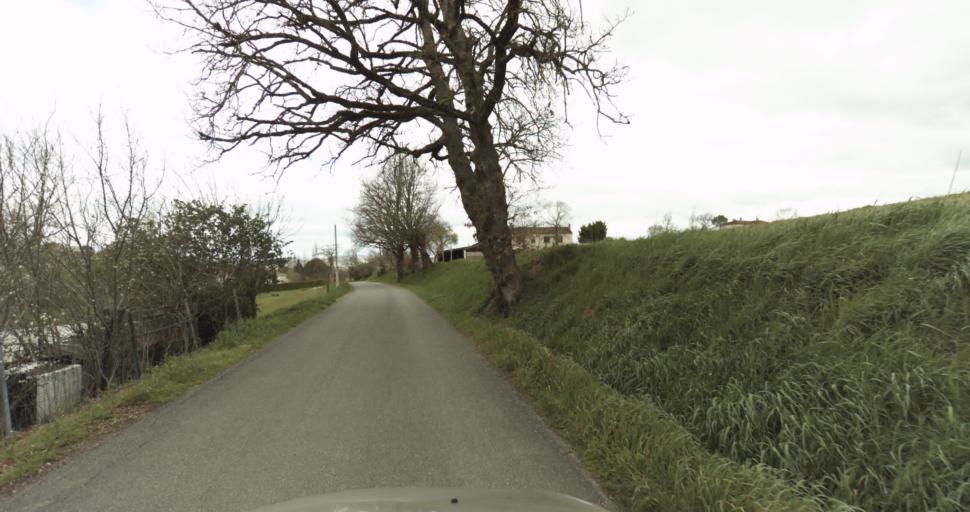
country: FR
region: Midi-Pyrenees
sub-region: Departement du Tarn
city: Puygouzon
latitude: 43.9028
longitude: 2.1702
